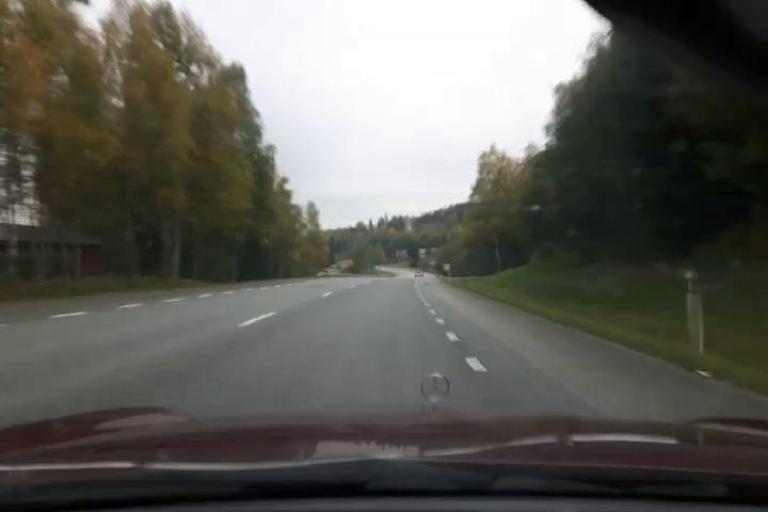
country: SE
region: Vaesternorrland
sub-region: Kramfors Kommun
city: Nordingra
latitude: 63.0120
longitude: 18.2903
